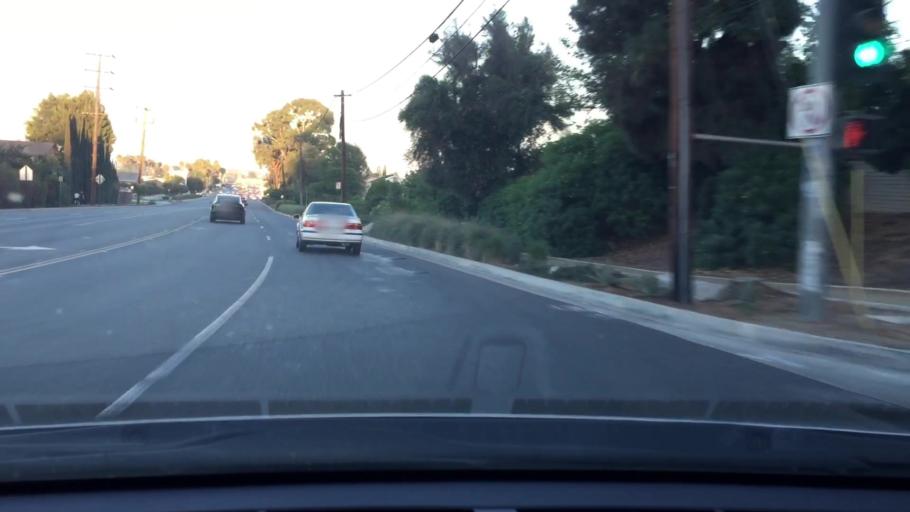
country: US
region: California
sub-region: San Bernardino County
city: Los Serranos
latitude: 33.9830
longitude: -117.7217
